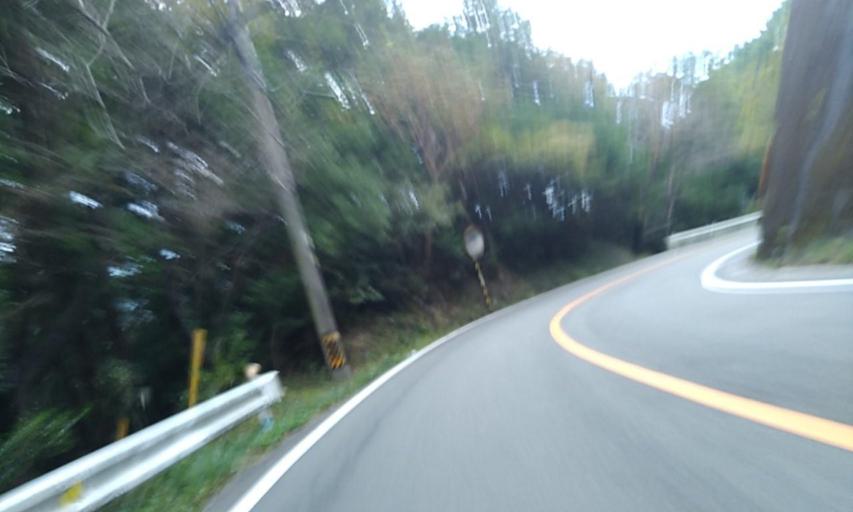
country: JP
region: Mie
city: Ise
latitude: 34.2887
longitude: 136.5354
